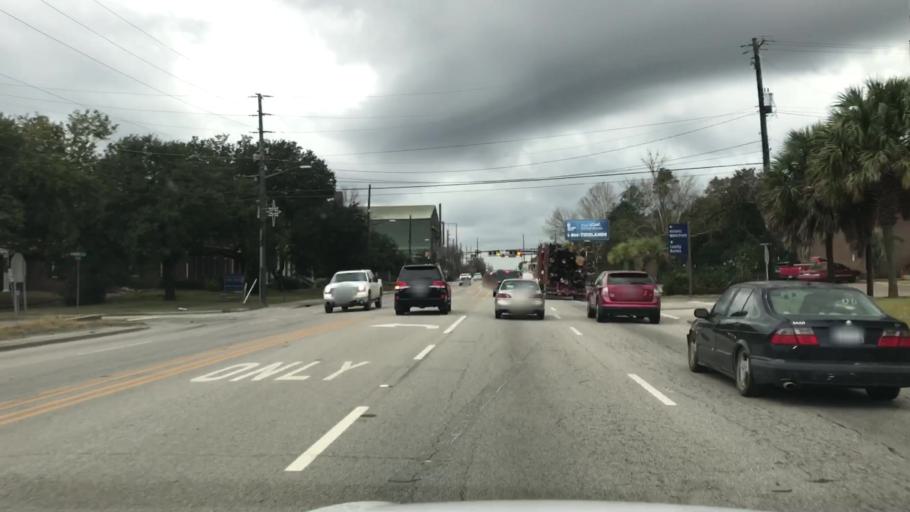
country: US
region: South Carolina
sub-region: Georgetown County
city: Georgetown
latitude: 33.3728
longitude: -79.2894
